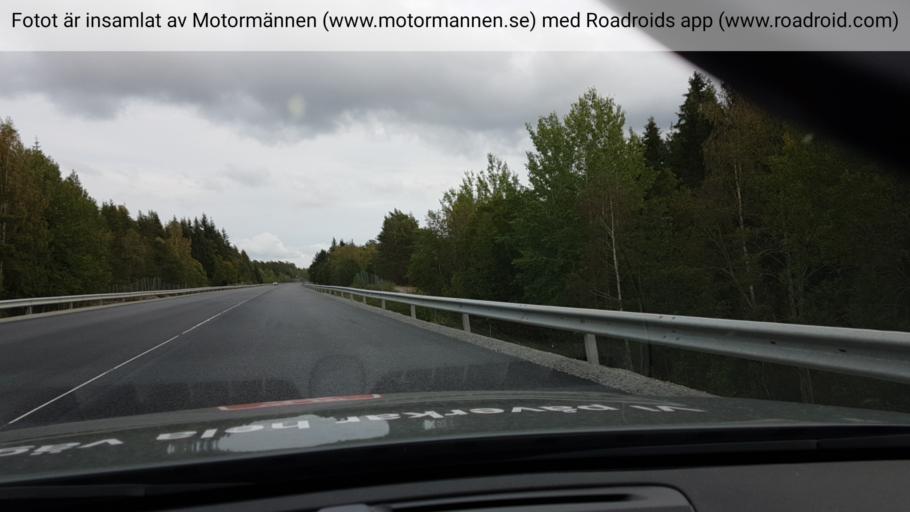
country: SE
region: Stockholm
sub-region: Norrtalje Kommun
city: Norrtalje
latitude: 59.7367
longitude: 18.7625
